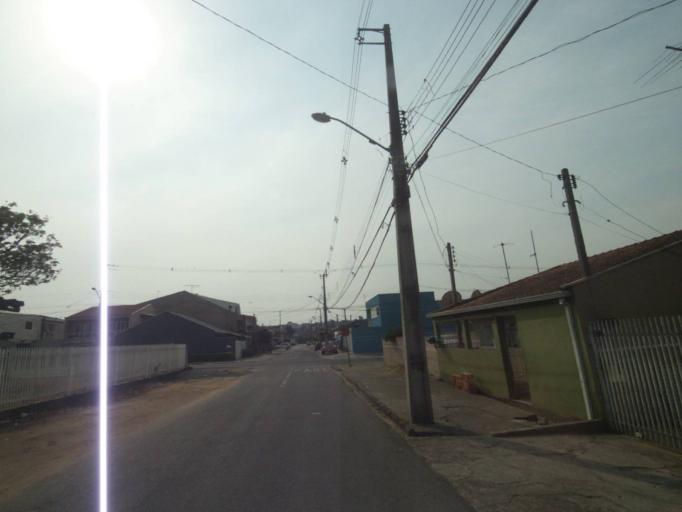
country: BR
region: Parana
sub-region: Sao Jose Dos Pinhais
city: Sao Jose dos Pinhais
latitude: -25.5255
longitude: -49.2731
